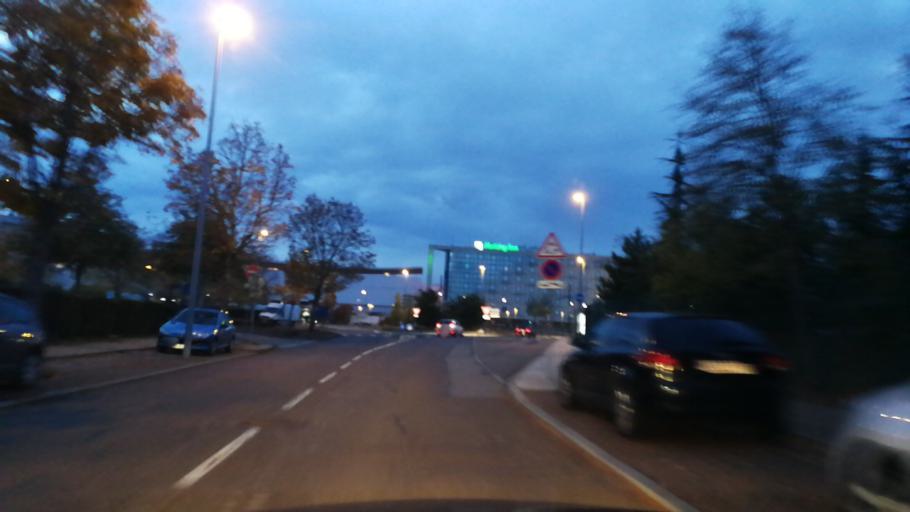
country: FR
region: Bourgogne
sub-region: Departement de la Cote-d'Or
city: Ruffey-les-Echirey
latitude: 47.3539
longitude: 5.0529
